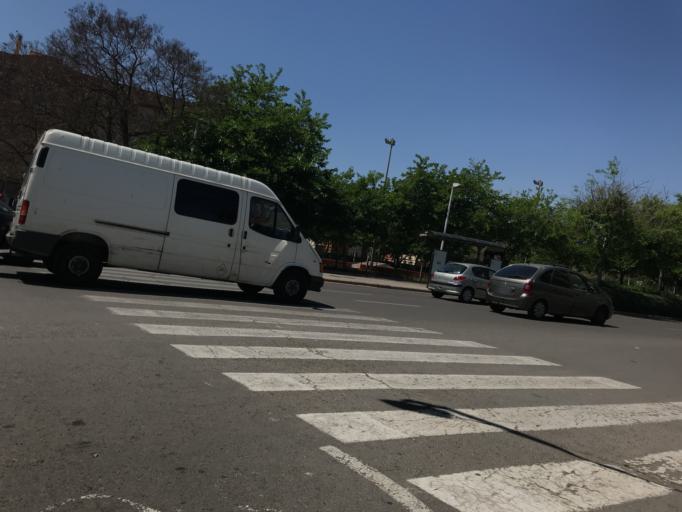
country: ES
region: Valencia
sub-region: Provincia de Valencia
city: Mislata
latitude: 39.4640
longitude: -0.4052
